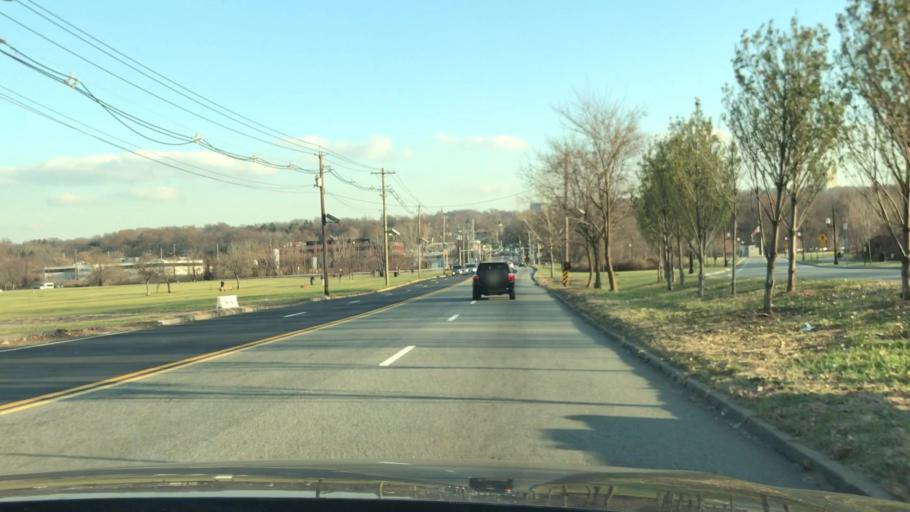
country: US
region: New Jersey
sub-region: Bergen County
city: Leonia
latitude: 40.8665
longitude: -73.9983
